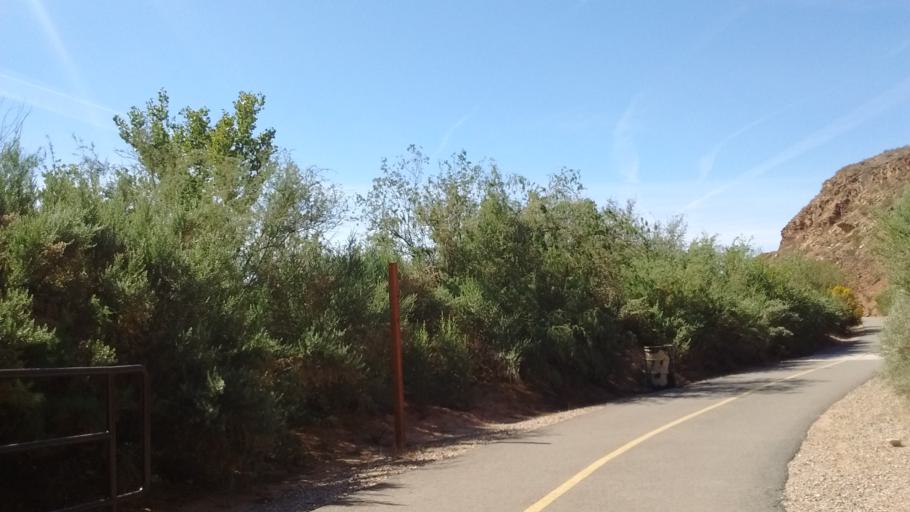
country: US
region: Utah
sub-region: Washington County
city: Washington
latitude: 37.1237
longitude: -113.4955
